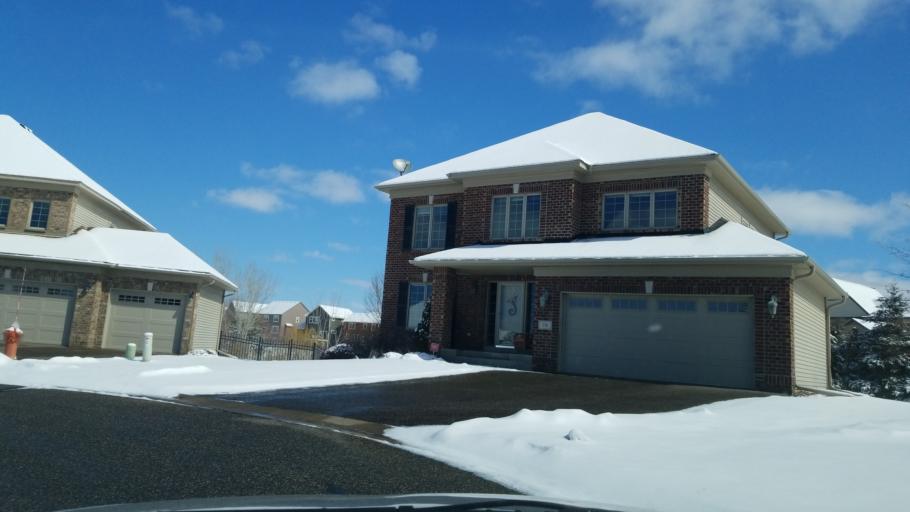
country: US
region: Wisconsin
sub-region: Saint Croix County
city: Hudson
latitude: 44.9531
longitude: -92.7013
